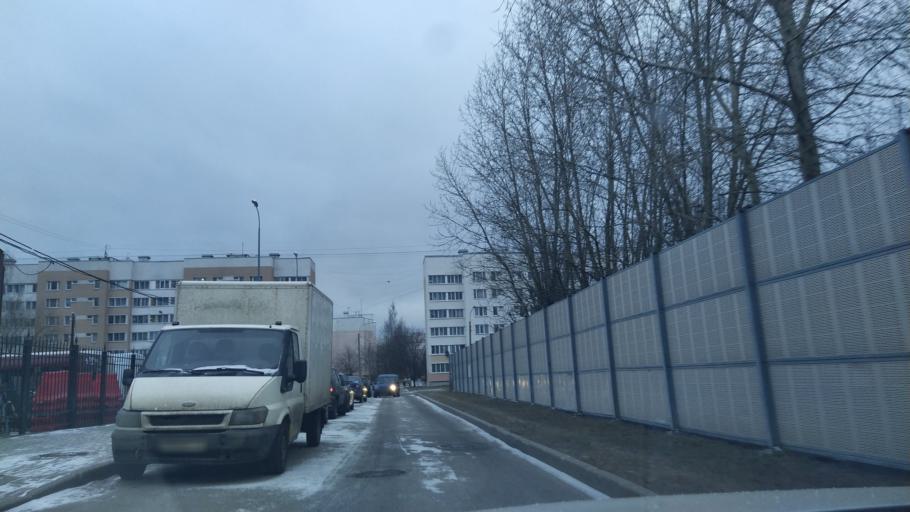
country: RU
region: St.-Petersburg
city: Pushkin
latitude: 59.7331
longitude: 30.4058
